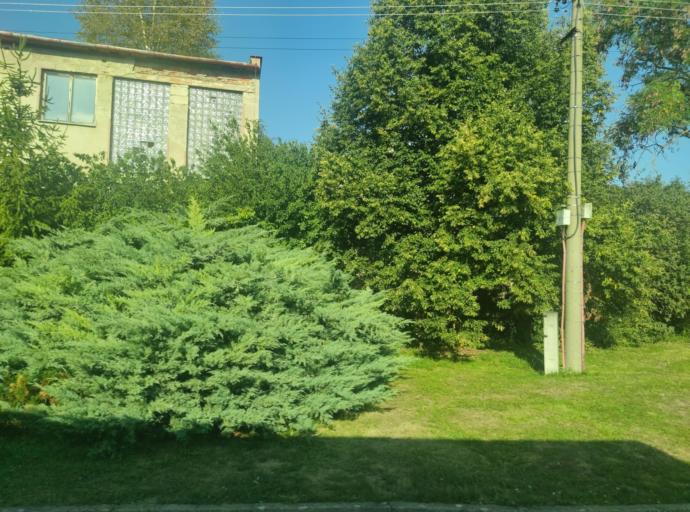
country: CZ
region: South Moravian
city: Vinicne Sumice
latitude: 49.1805
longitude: 16.8470
